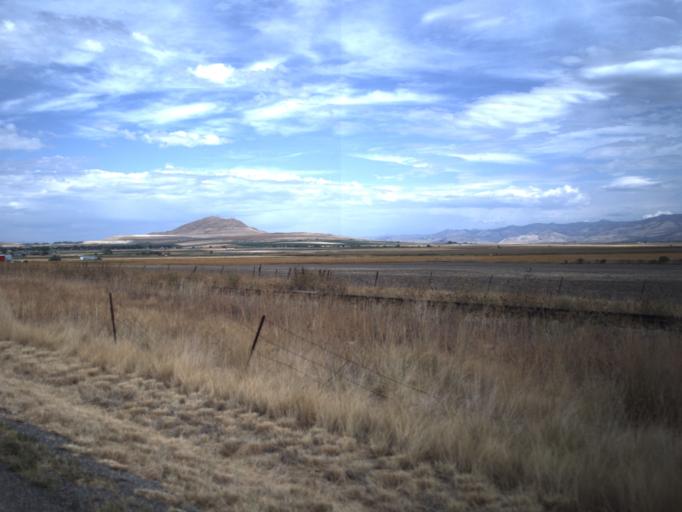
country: US
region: Utah
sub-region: Cache County
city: Benson
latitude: 41.8104
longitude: -111.9950
